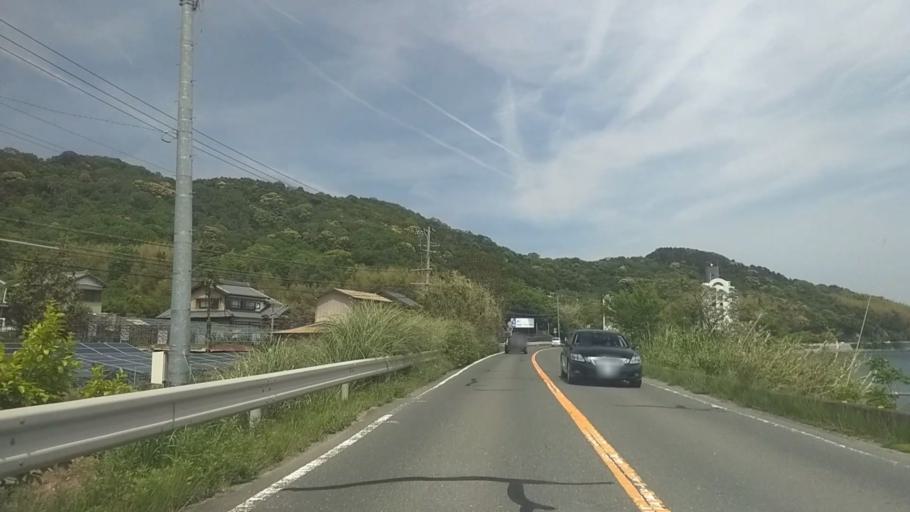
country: JP
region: Shizuoka
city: Kosai-shi
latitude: 34.7685
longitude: 137.5368
